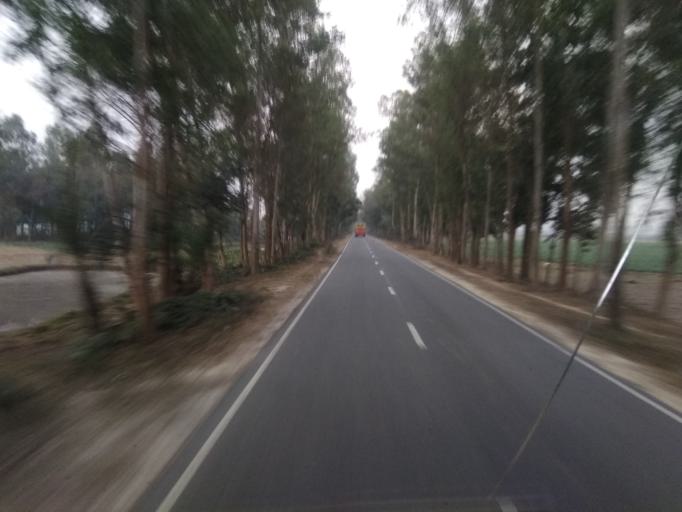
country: BD
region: Rajshahi
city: Bogra
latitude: 24.6864
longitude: 89.2924
